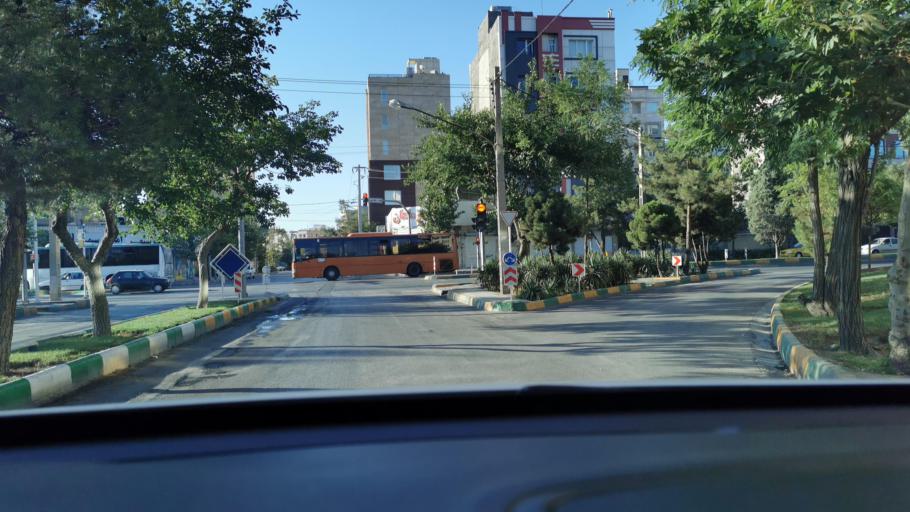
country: IR
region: Razavi Khorasan
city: Mashhad
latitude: 36.3589
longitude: 59.4912
